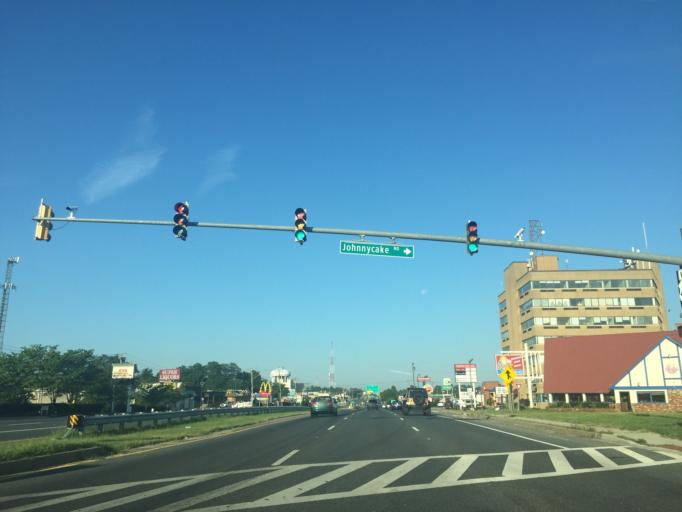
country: US
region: Maryland
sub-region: Baltimore County
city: Catonsville
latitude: 39.2898
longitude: -76.7250
